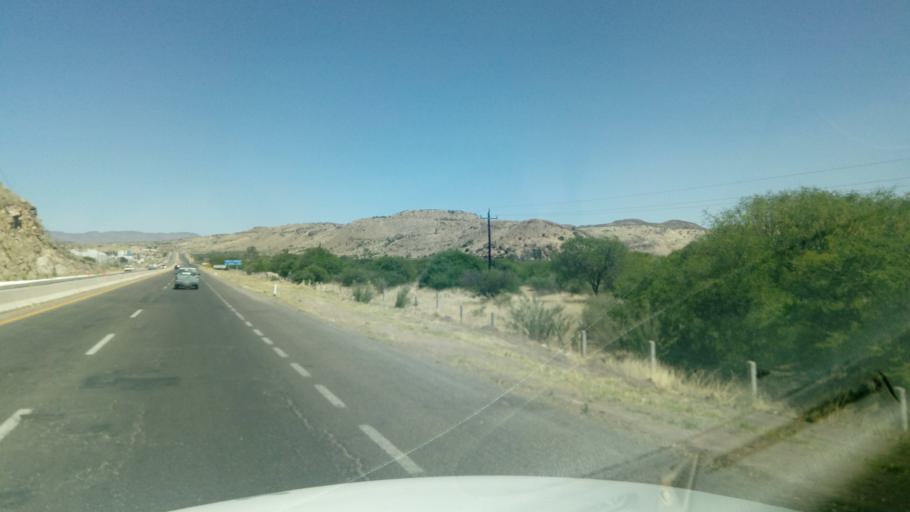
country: MX
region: Durango
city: Victoria de Durango
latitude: 24.0928
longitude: -104.6838
